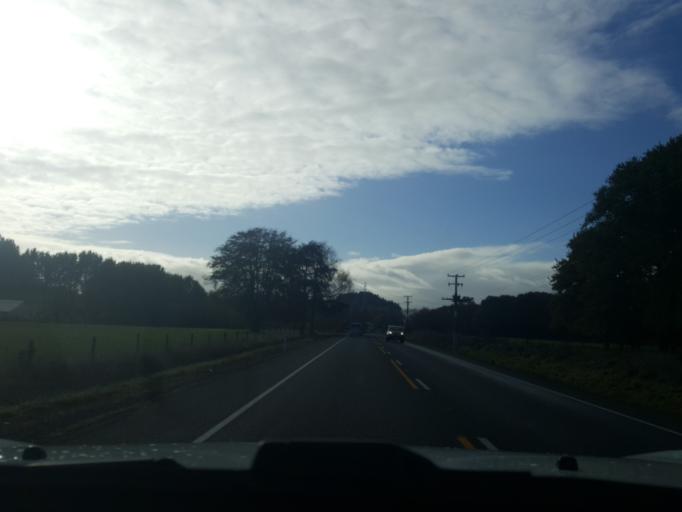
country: NZ
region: Waikato
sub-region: Waipa District
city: Cambridge
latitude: -37.6666
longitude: 175.4939
